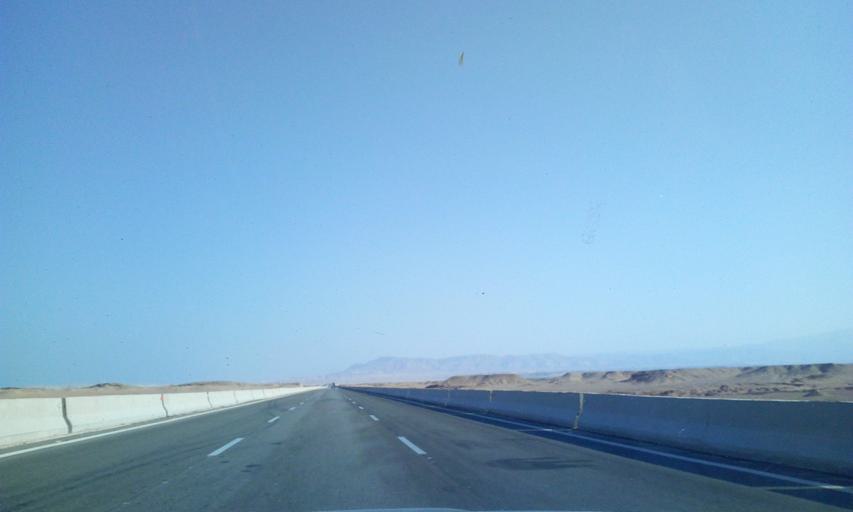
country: EG
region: As Suways
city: Ain Sukhna
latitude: 29.1495
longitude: 32.5160
